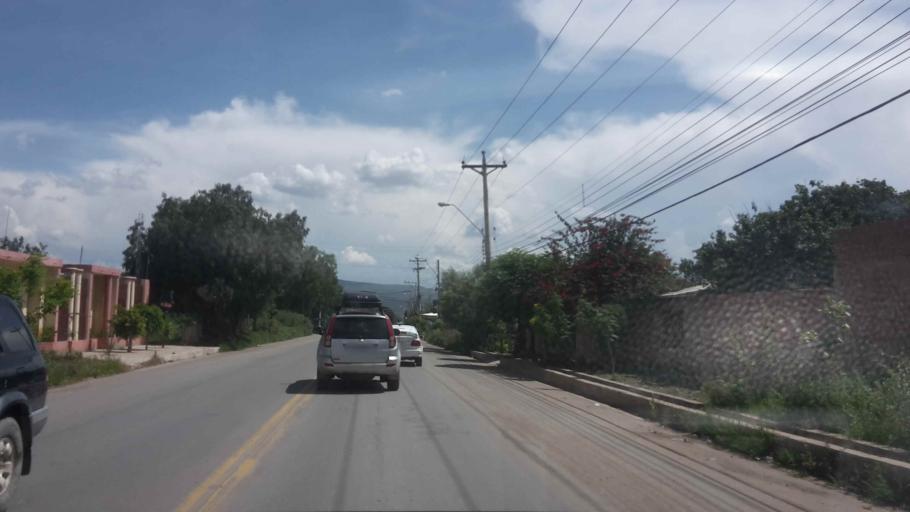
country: BO
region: Cochabamba
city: Cochabamba
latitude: -17.3673
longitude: -66.2310
